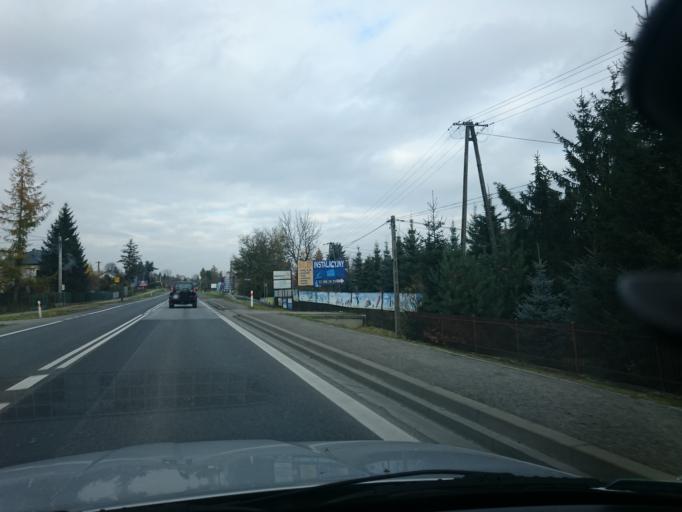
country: PL
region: Lesser Poland Voivodeship
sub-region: Powiat krakowski
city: Michalowice
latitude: 50.1624
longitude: 19.9794
